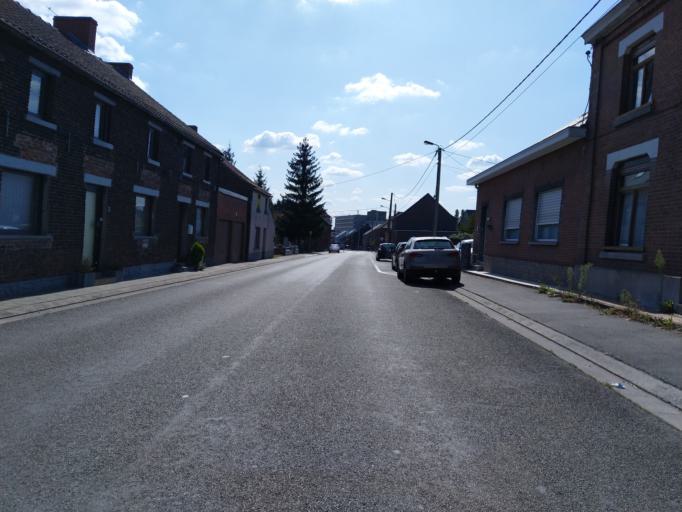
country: BE
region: Wallonia
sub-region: Province du Hainaut
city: Saint-Ghislain
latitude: 50.4741
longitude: 3.8417
